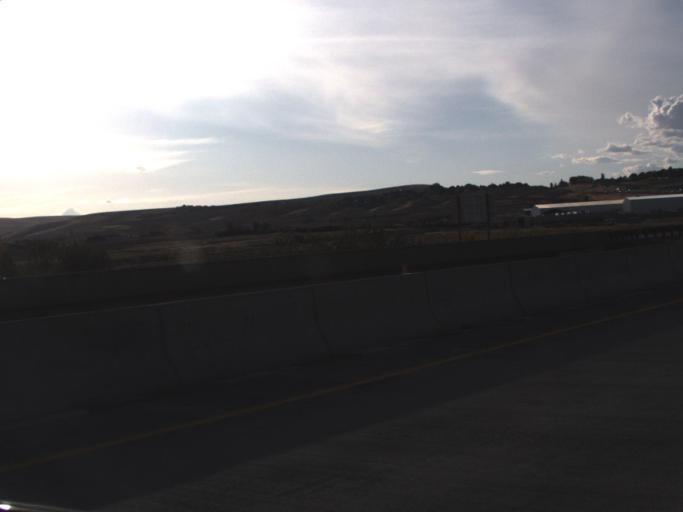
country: US
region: Washington
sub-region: Benton County
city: Richland
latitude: 46.1943
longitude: -119.2681
